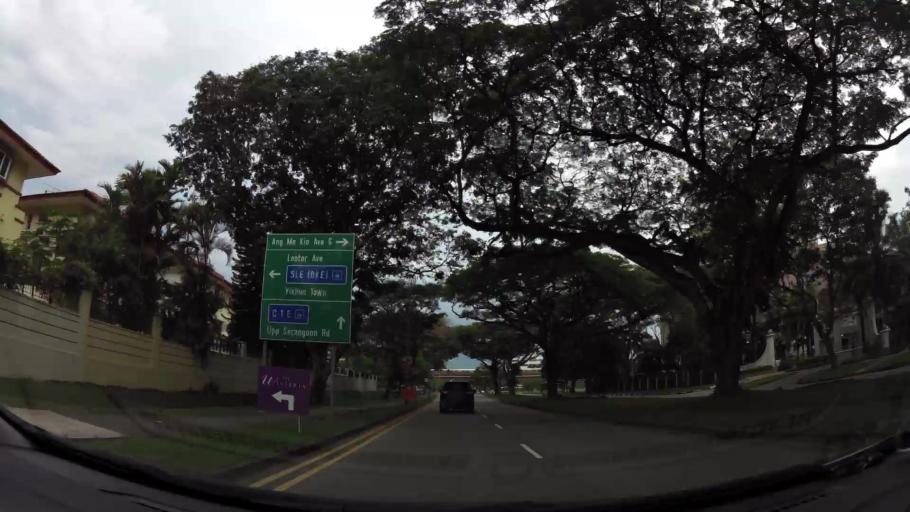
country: MY
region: Johor
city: Kampung Pasir Gudang Baru
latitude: 1.3869
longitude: 103.8403
